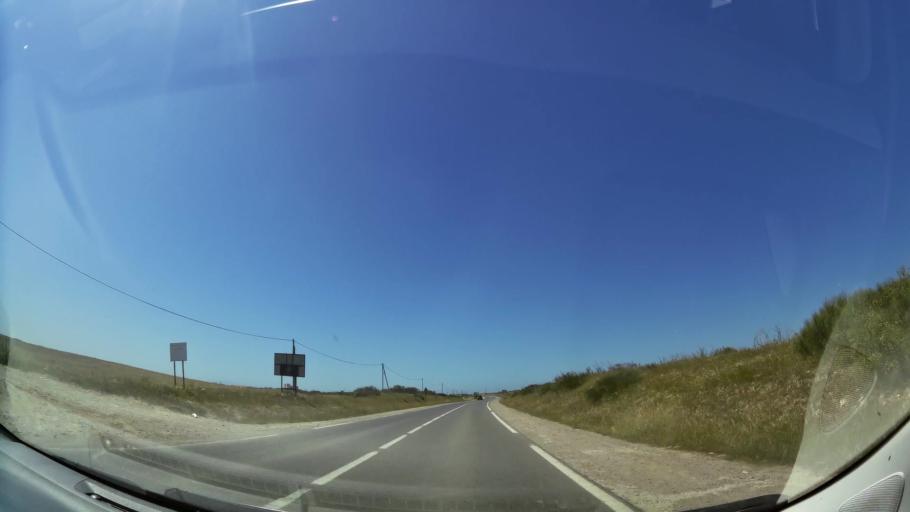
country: MA
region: Oriental
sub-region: Berkane-Taourirt
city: Madagh
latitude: 35.1285
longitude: -2.3948
